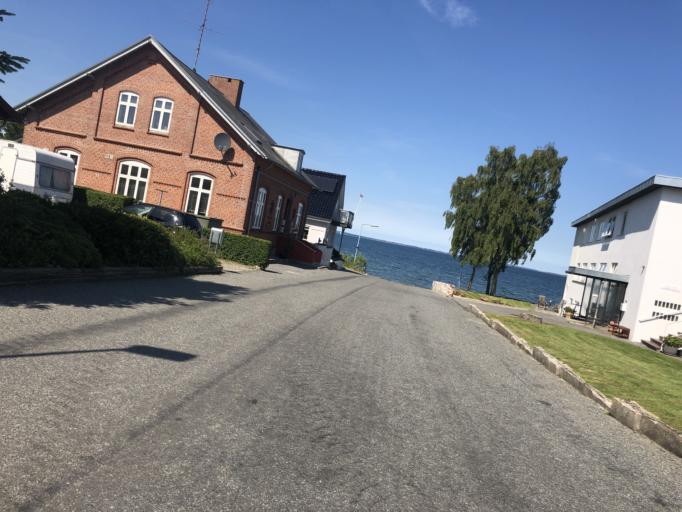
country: DK
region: South Denmark
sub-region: AEro Kommune
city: Marstal
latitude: 54.8605
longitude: 10.5166
